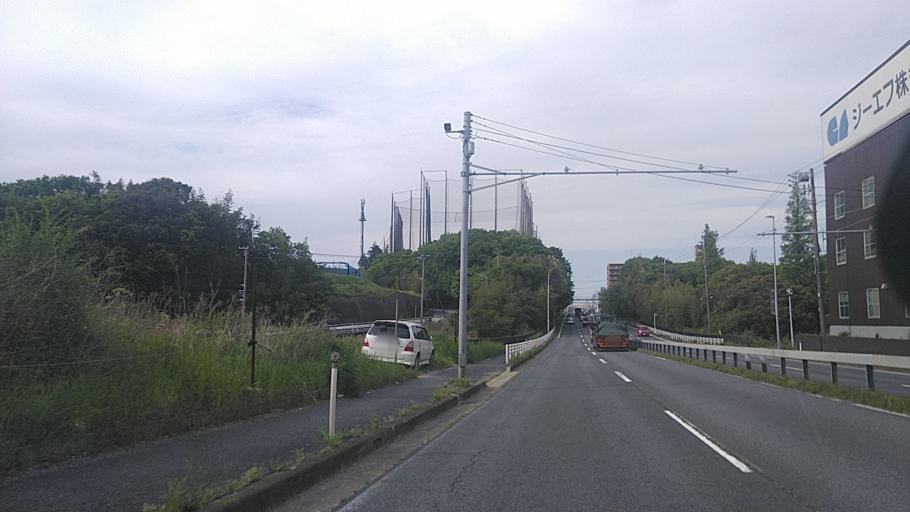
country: JP
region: Chiba
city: Shiroi
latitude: 35.7322
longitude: 140.1193
